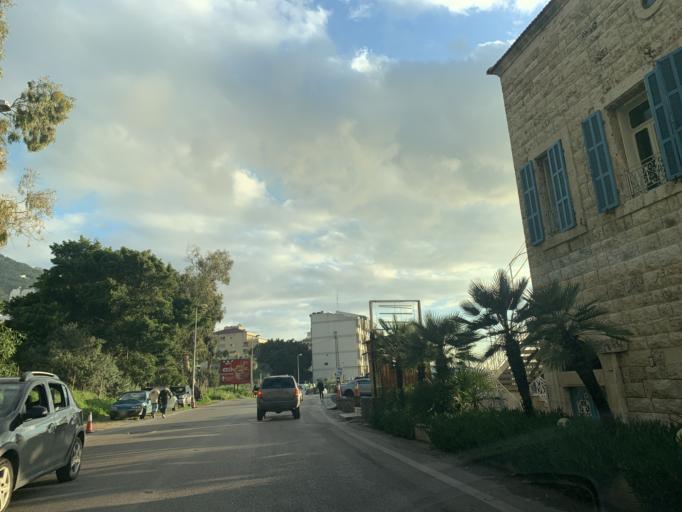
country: LB
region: Mont-Liban
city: Djounie
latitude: 33.9979
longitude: 35.6438
